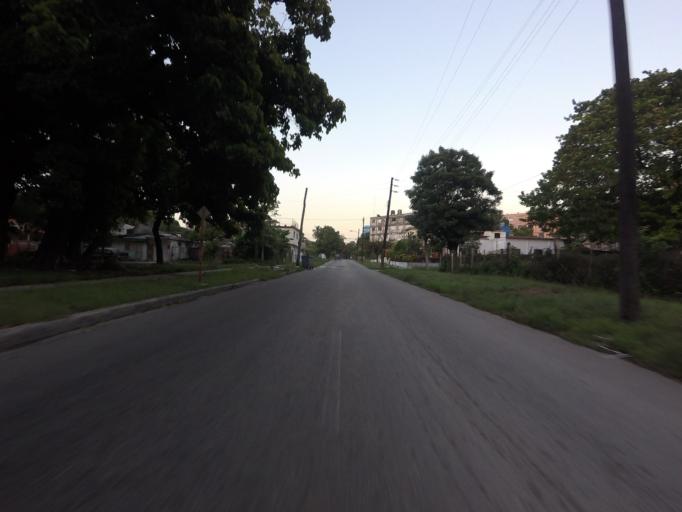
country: CU
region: La Habana
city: Havana
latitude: 23.1244
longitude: -82.3893
